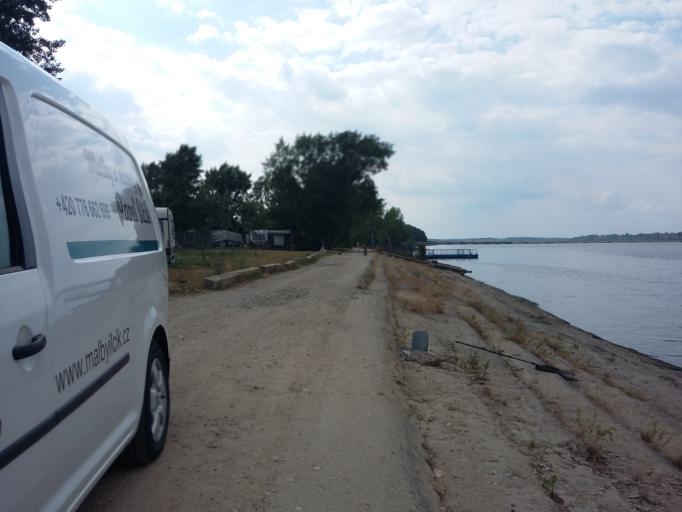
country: CZ
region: South Moravian
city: Sakvice
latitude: 48.8868
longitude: 16.6568
